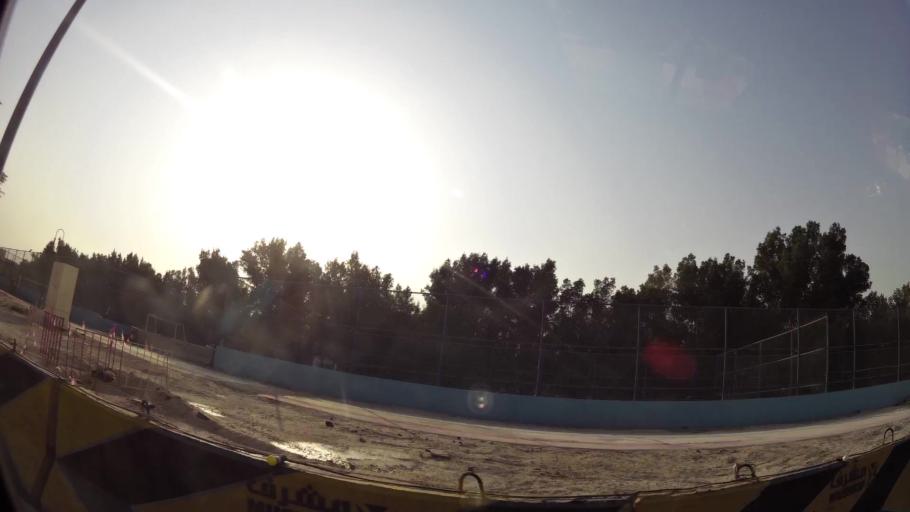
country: KW
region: Muhafazat Hawalli
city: Ar Rumaythiyah
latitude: 29.3193
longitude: 48.0875
